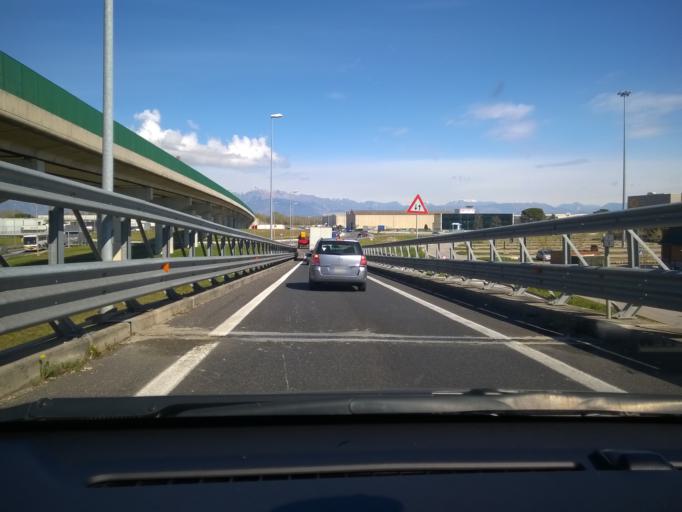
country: IT
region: Friuli Venezia Giulia
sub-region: Provincia di Pordenone
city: Fiume Veneto
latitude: 45.9444
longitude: 12.7208
